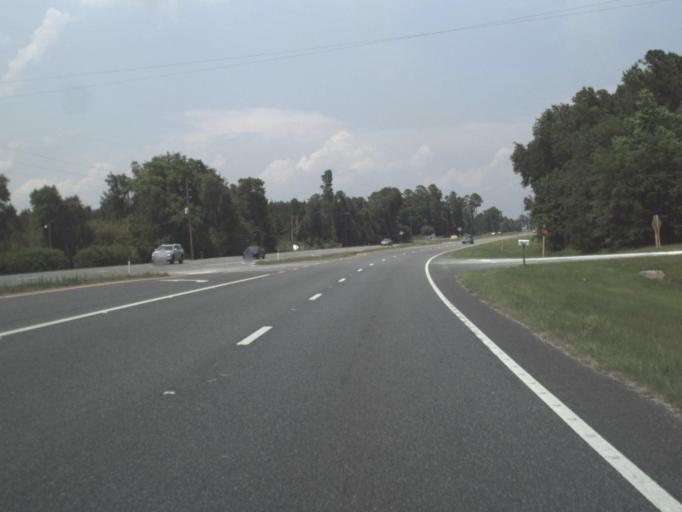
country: US
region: Florida
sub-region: Putnam County
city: Palatka
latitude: 29.7043
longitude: -81.6637
